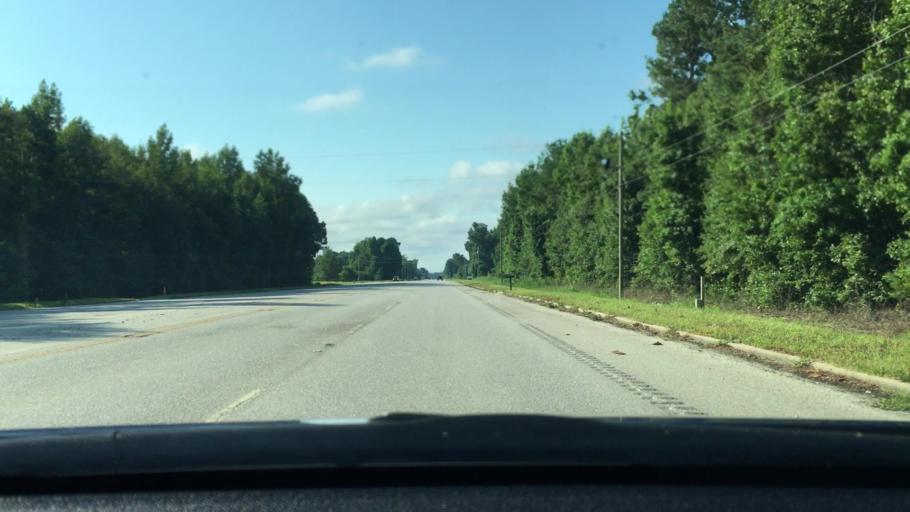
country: US
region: South Carolina
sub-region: Clarendon County
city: Manning
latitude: 33.7699
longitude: -80.2359
